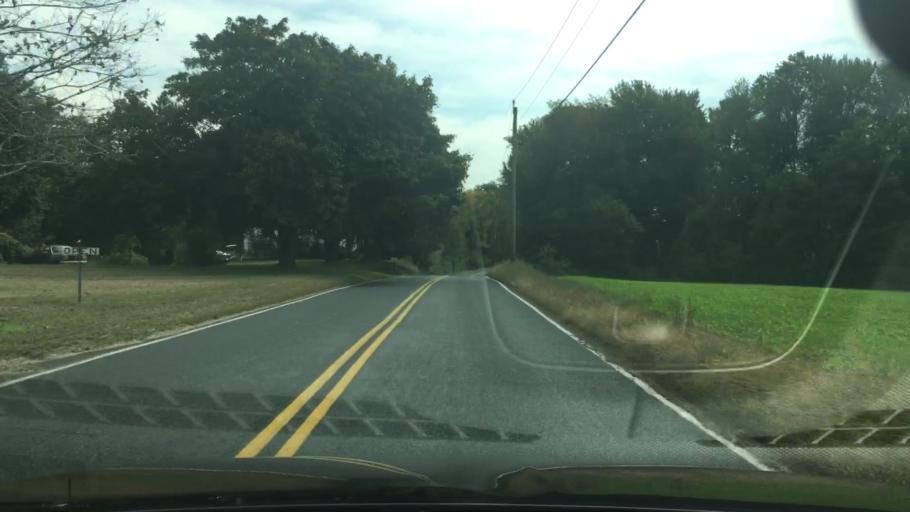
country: US
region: Connecticut
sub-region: Hartford County
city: Hazardville
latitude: 41.9934
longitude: -72.4954
